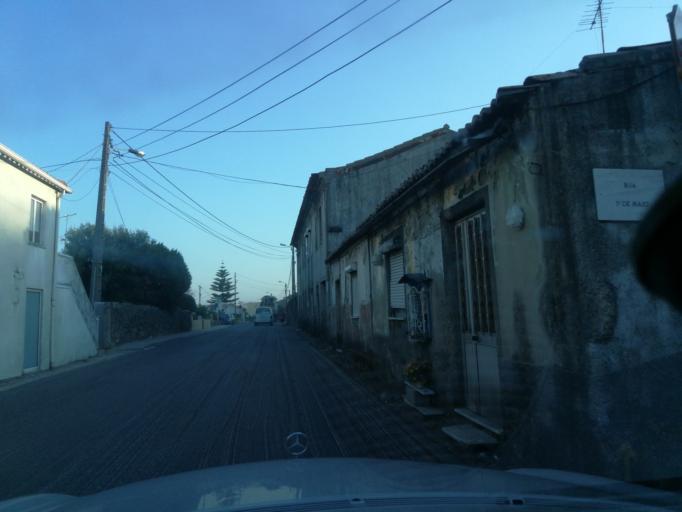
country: PT
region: Braga
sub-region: Braga
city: Braga
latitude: 41.5339
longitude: -8.4301
